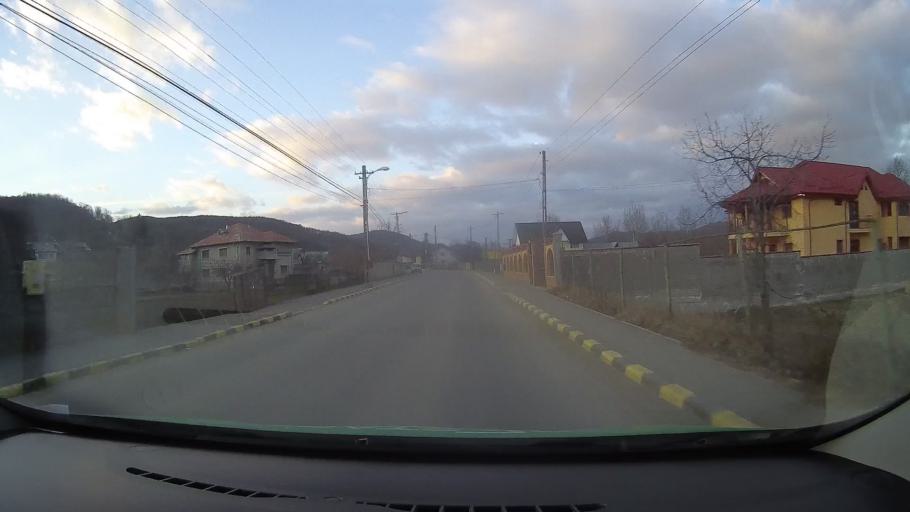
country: RO
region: Dambovita
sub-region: Municipiul Moreni
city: Moreni
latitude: 44.9884
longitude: 25.6381
